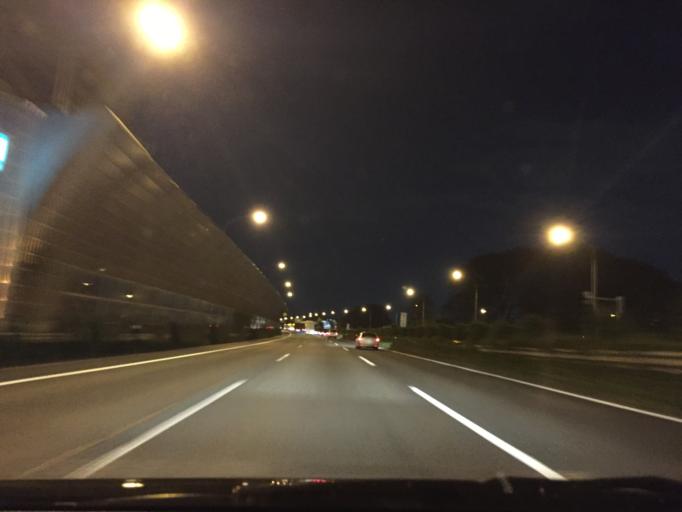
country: JP
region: Tokyo
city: Chofugaoka
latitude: 35.5873
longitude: 139.5677
